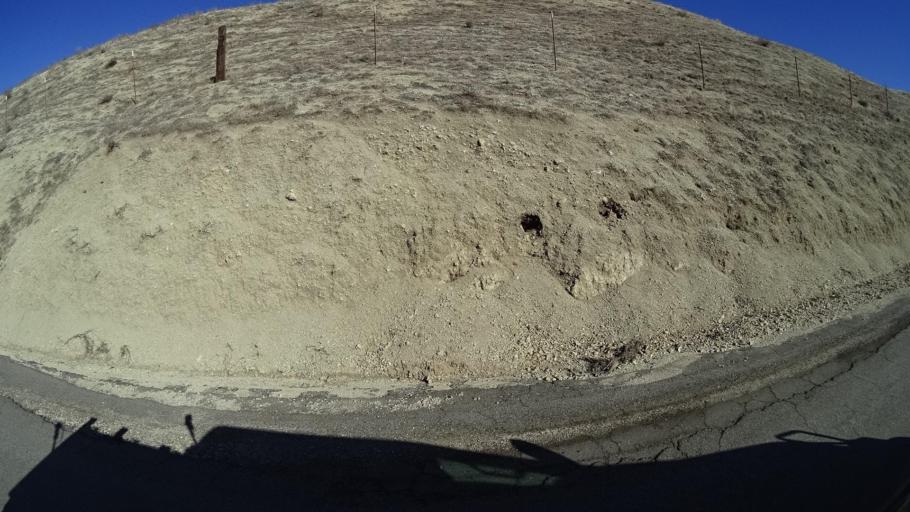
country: US
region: California
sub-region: Kern County
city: Maricopa
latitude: 34.9580
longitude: -119.4093
